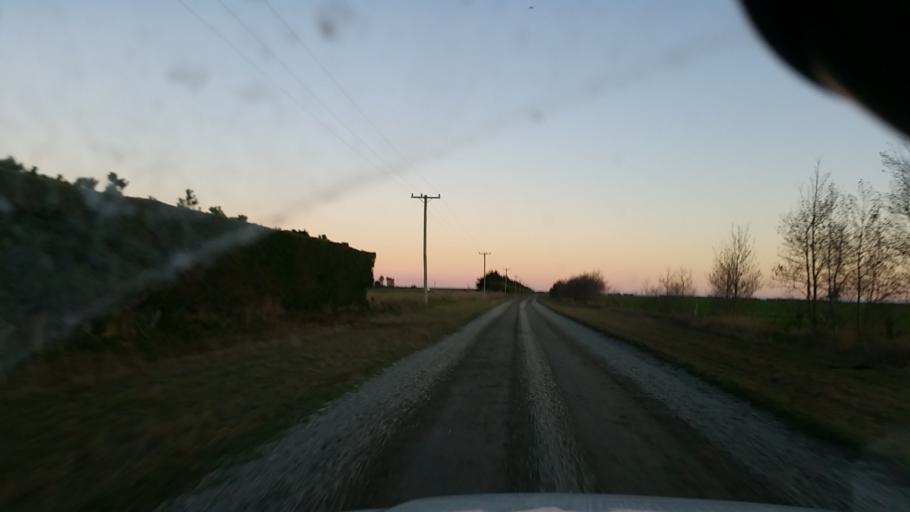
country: NZ
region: Canterbury
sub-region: Ashburton District
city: Tinwald
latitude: -44.0767
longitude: 171.6636
